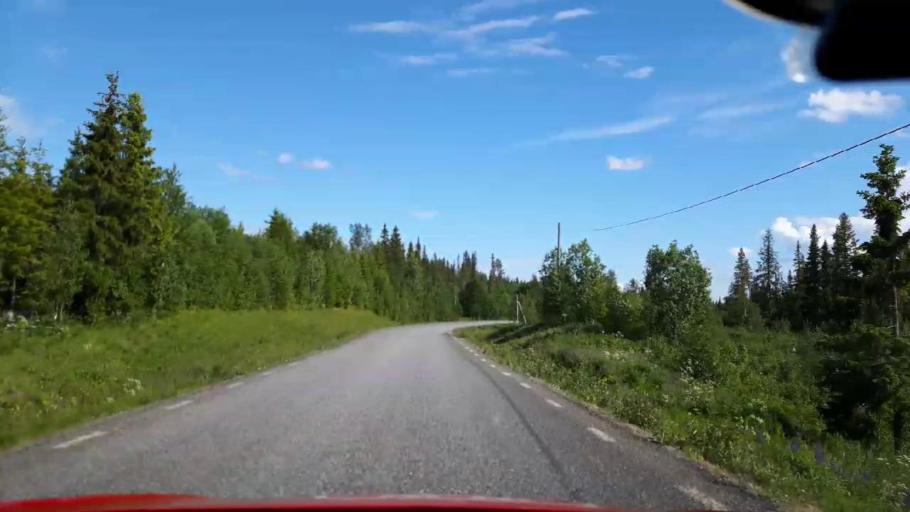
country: SE
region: Jaemtland
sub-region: Krokoms Kommun
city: Valla
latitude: 63.7102
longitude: 14.1396
